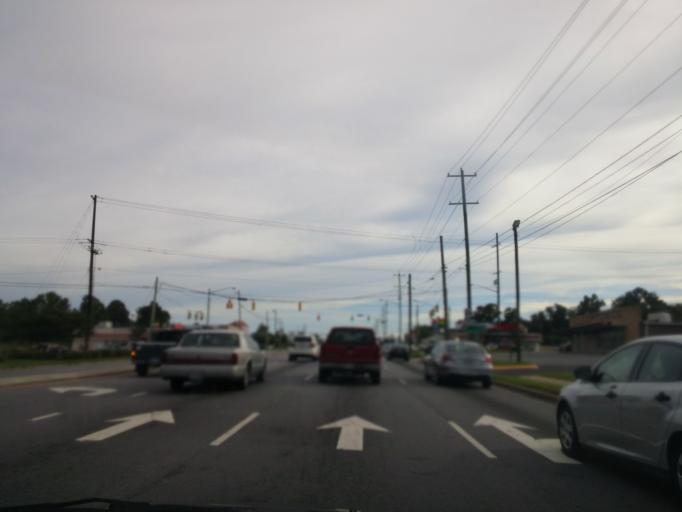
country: US
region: North Carolina
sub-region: Pitt County
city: Greenville
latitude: 35.6138
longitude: -77.3928
